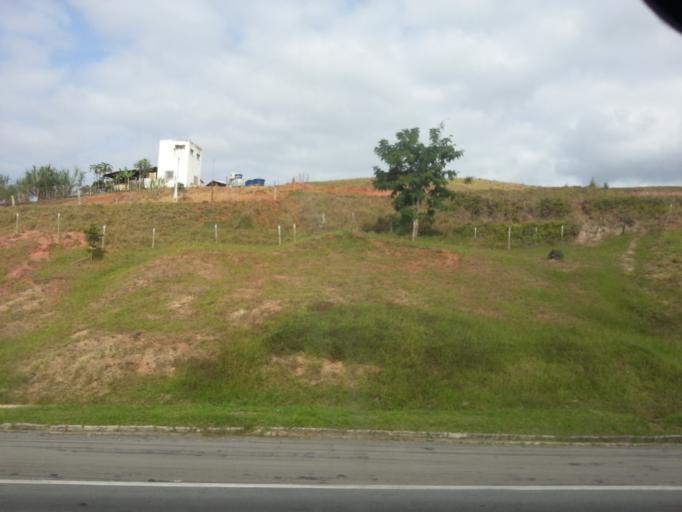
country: BR
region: Sao Paulo
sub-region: Santa Isabel
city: Santa Isabel
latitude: -23.3496
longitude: -46.1733
